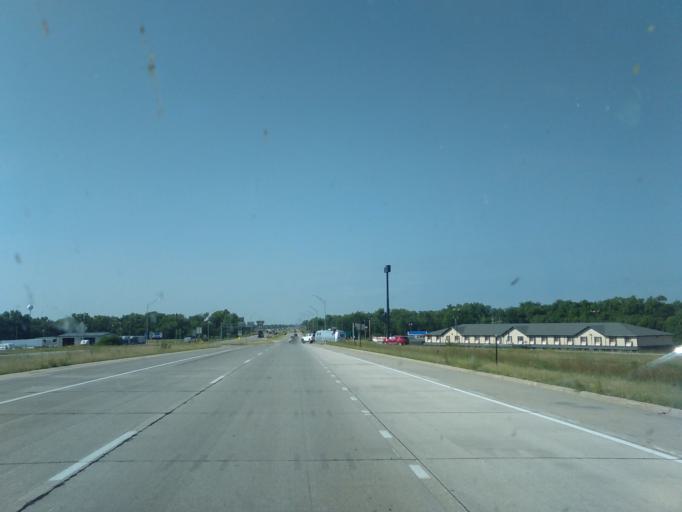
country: US
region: Nebraska
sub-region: Hall County
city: Grand Island
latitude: 40.8212
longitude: -98.3784
